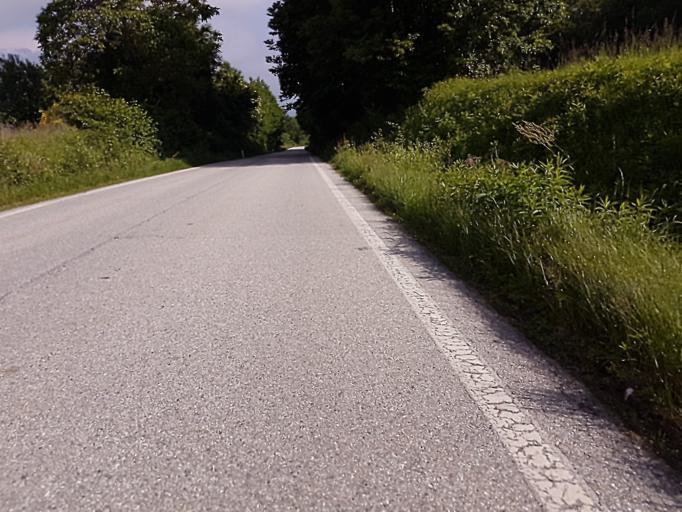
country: IT
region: Piedmont
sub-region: Provincia di Torino
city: Vialfre
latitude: 45.3862
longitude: 7.8172
